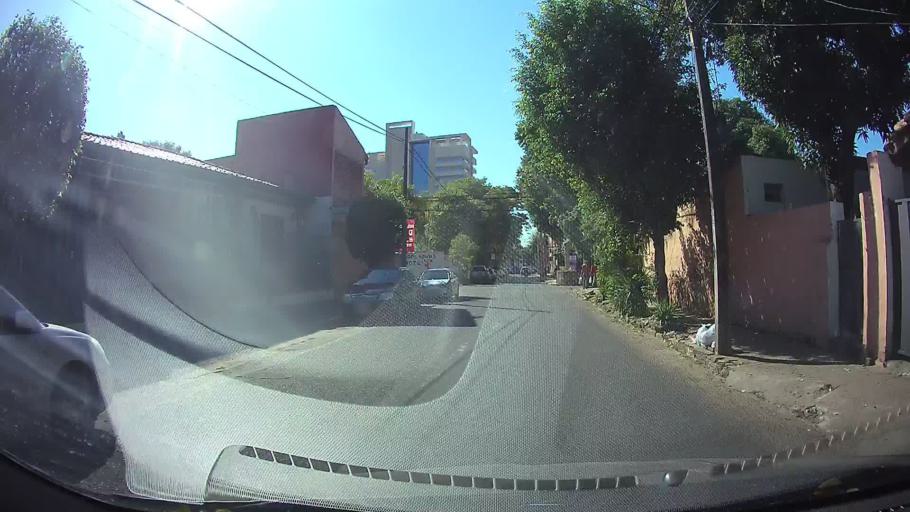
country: PY
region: Central
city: Fernando de la Mora
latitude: -25.3028
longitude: -57.5665
